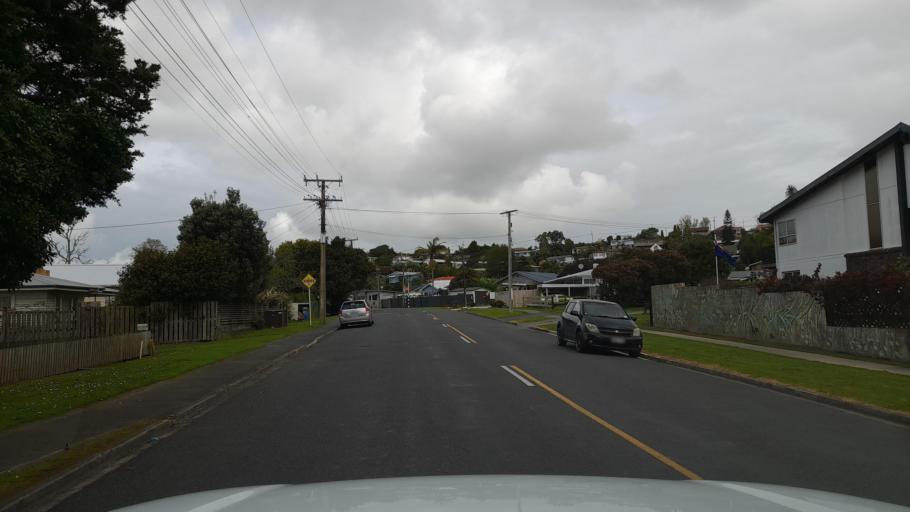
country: NZ
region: Northland
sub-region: Whangarei
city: Whangarei
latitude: -35.7349
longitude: 174.3211
